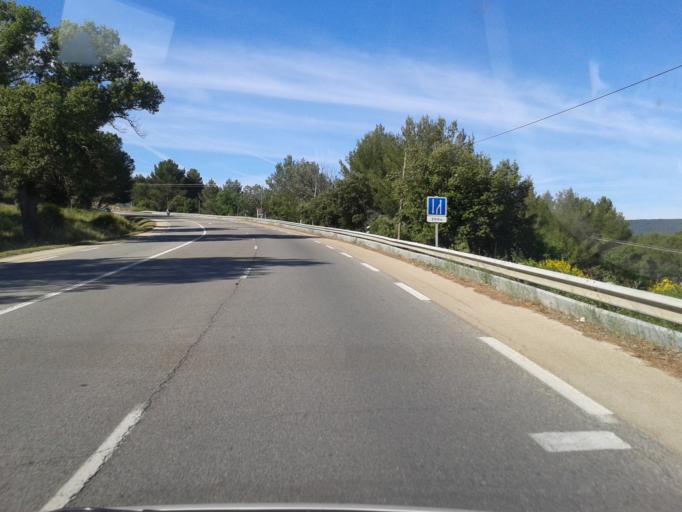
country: FR
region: Provence-Alpes-Cote d'Azur
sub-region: Departement des Bouches-du-Rhone
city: Meyrargues
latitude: 43.6385
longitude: 5.5176
